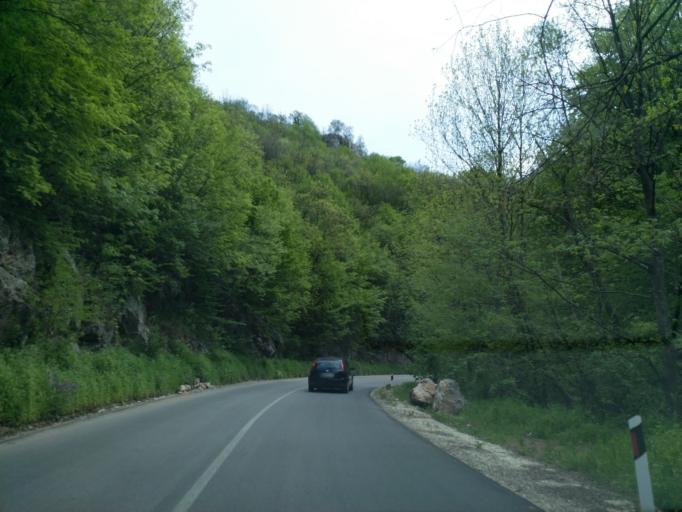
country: RS
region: Central Serbia
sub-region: Pomoravski Okrug
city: Despotovac
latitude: 43.9705
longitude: 21.5250
